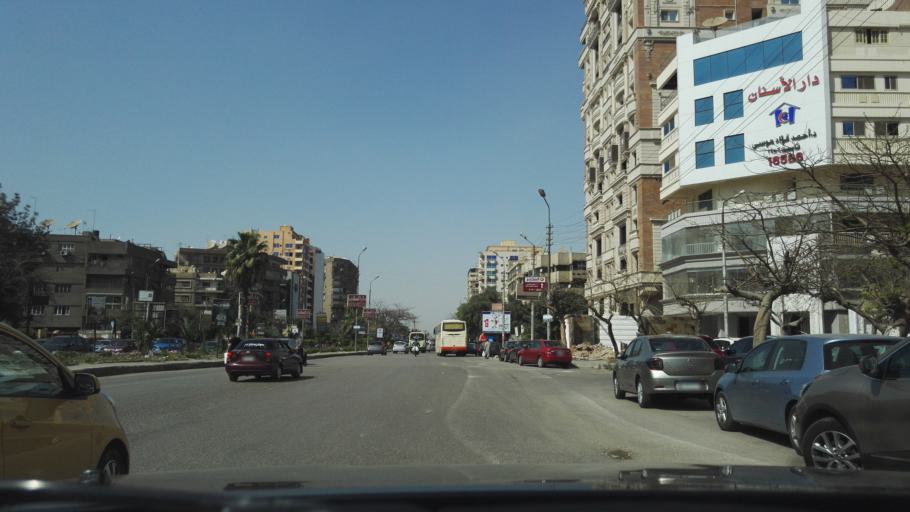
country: EG
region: Muhafazat al Qahirah
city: Cairo
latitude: 30.0865
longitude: 31.3411
